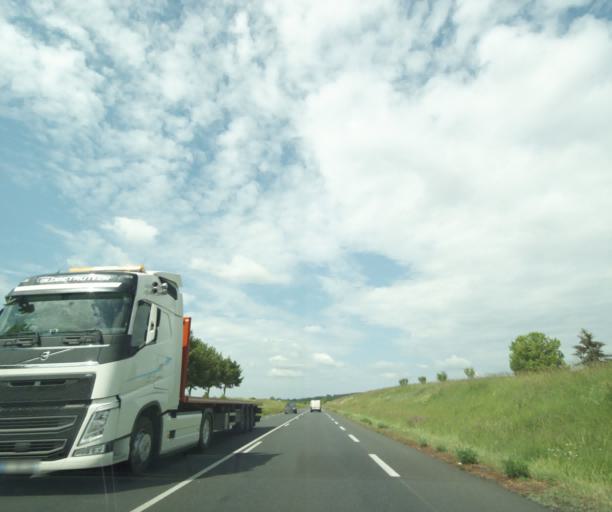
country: FR
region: Pays de la Loire
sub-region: Departement de Maine-et-Loire
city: Distre
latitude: 47.2248
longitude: -0.1163
